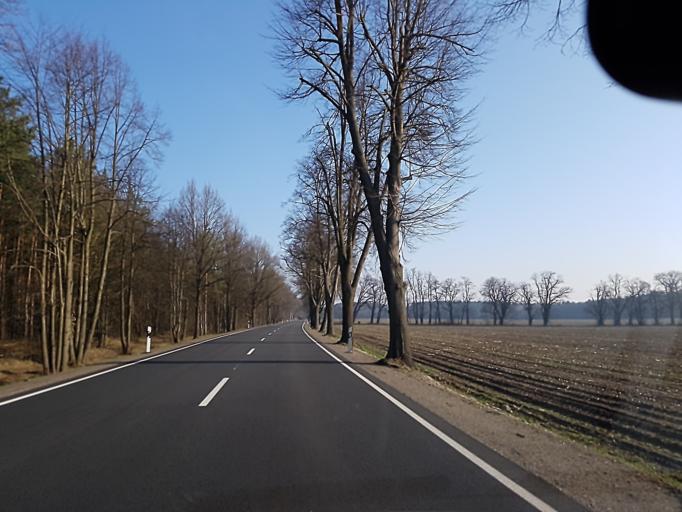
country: DE
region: Brandenburg
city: Bronkow
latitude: 51.6824
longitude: 13.9149
